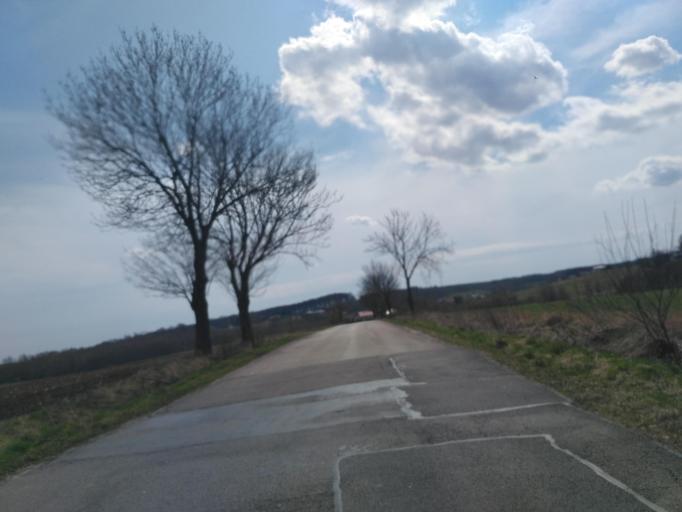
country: PL
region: Subcarpathian Voivodeship
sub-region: Powiat ropczycko-sedziszowski
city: Sedziszow Malopolski
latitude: 50.0527
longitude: 21.7151
